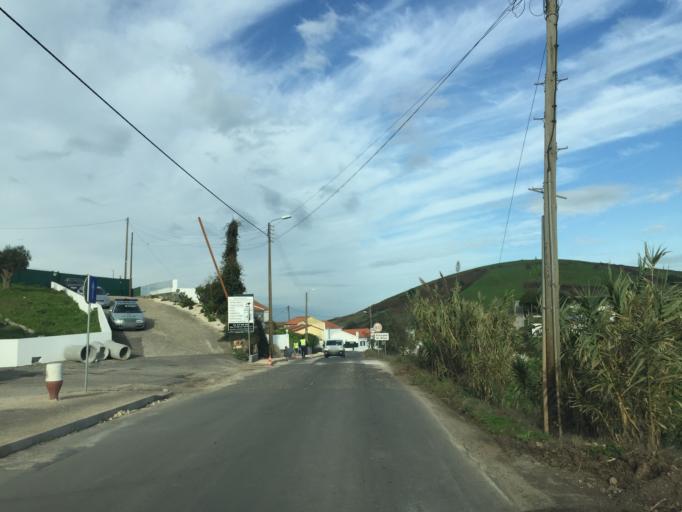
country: PT
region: Lisbon
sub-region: Sintra
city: Almargem
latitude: 38.8494
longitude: -9.2630
